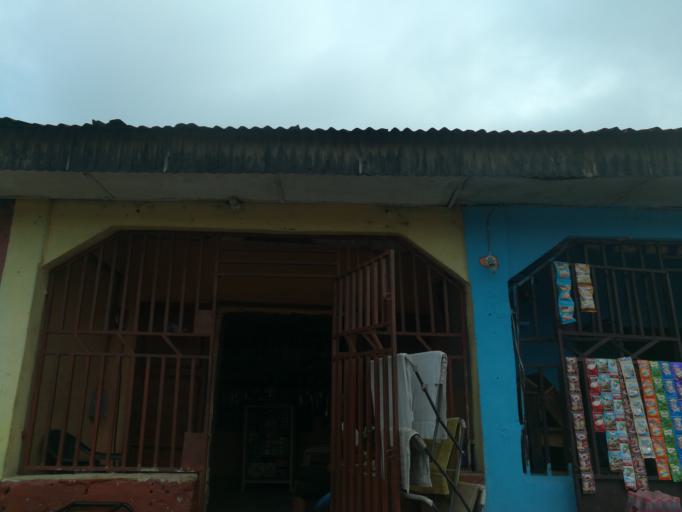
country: NG
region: Rivers
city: Port Harcourt
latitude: 4.8770
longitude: 6.9857
